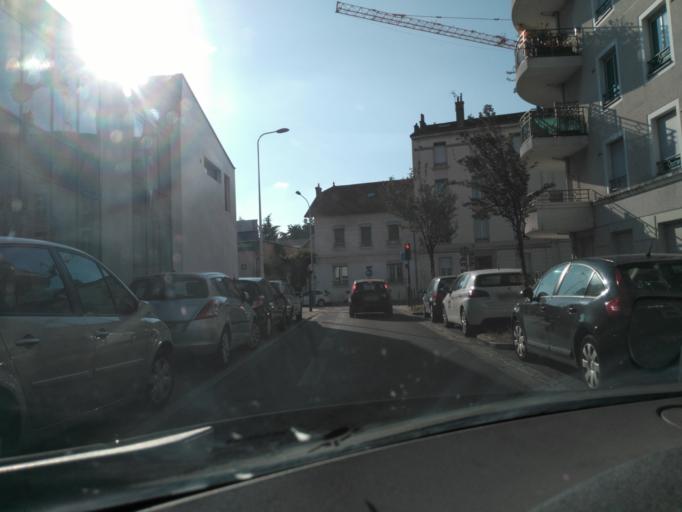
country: FR
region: Rhone-Alpes
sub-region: Departement du Rhone
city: Lyon
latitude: 45.7420
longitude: 4.8697
